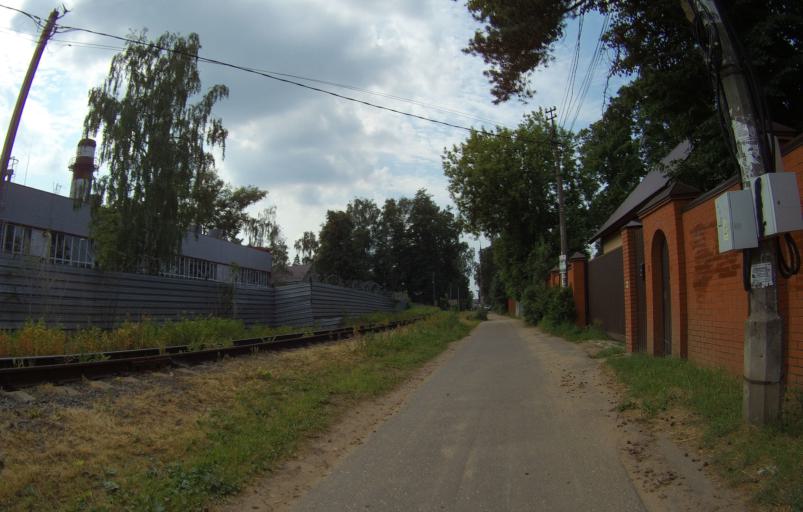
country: RU
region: Moskovskaya
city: Bykovo
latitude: 55.6214
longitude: 38.0708
